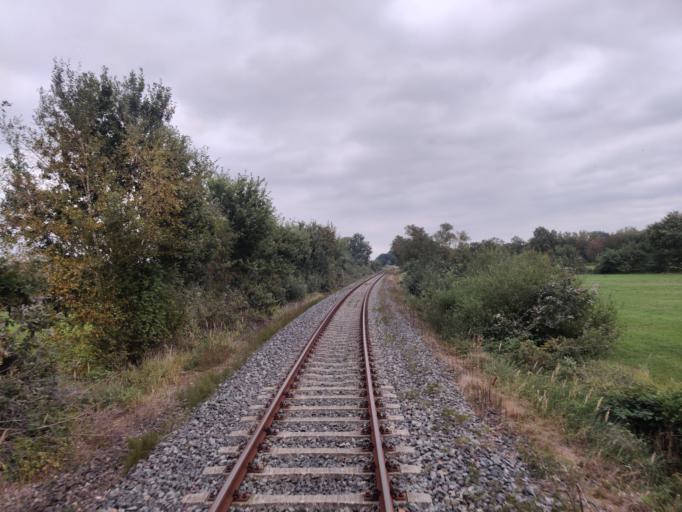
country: DE
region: Lower Saxony
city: Gnarrenburg
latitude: 53.3356
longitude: 8.9836
